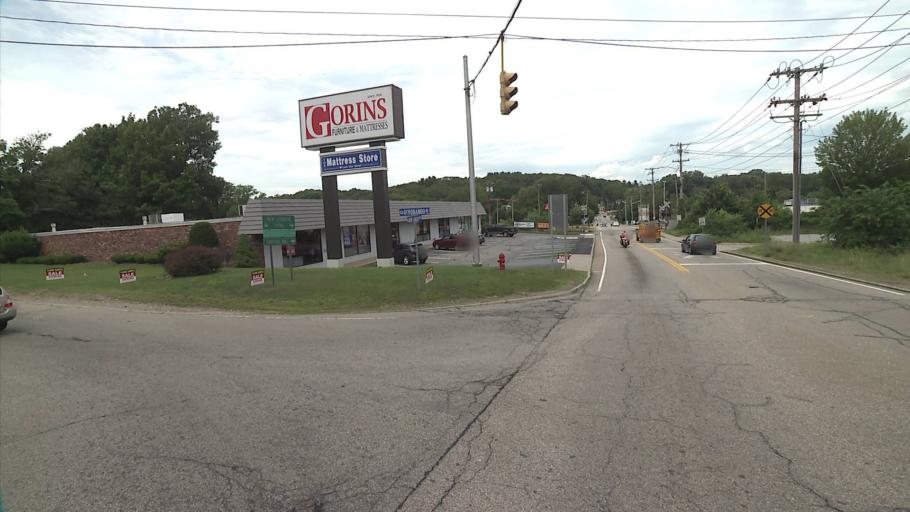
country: US
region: Connecticut
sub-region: New London County
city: Norwich
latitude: 41.5449
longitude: -72.0956
